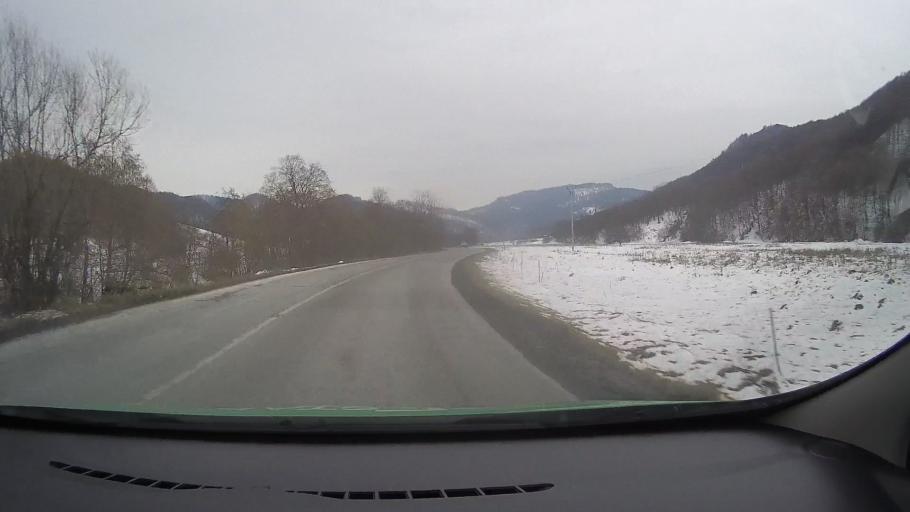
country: RO
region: Brasov
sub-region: Oras Rasnov
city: Rasnov
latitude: 45.5475
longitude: 25.4962
